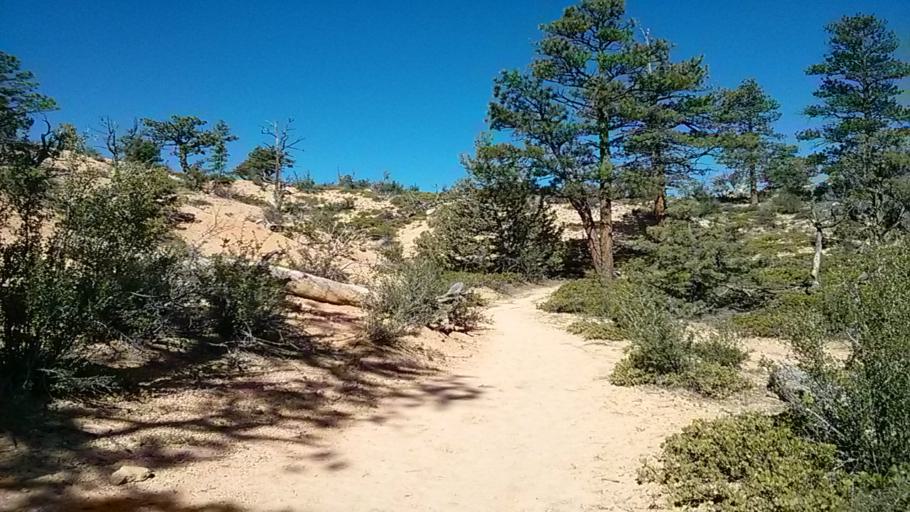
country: US
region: Utah
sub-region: Garfield County
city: Panguitch
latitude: 37.6359
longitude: -112.1333
